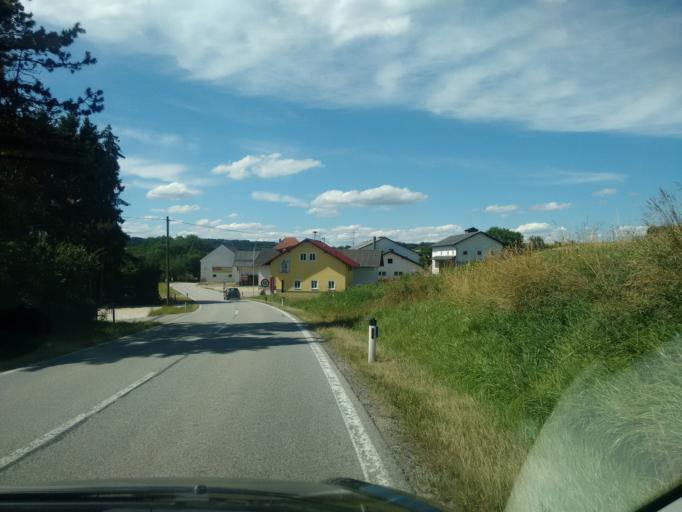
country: AT
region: Upper Austria
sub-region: Politischer Bezirk Ried im Innkreis
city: Ried im Innkreis
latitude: 48.2176
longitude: 13.4125
